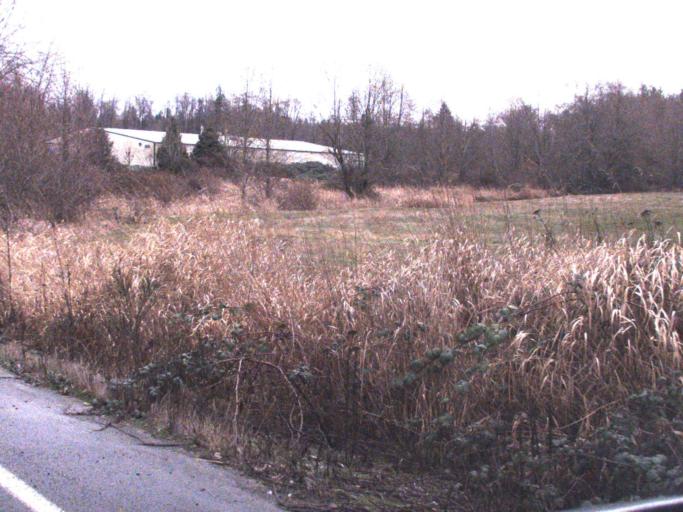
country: US
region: Washington
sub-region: Snohomish County
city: Sisco Heights
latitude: 48.1516
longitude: -122.1177
